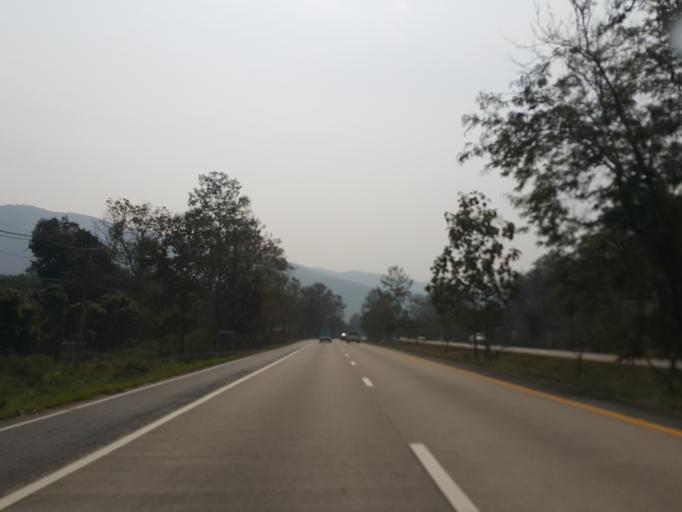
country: TH
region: Lamphun
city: Mae Tha
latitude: 18.5081
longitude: 99.1297
